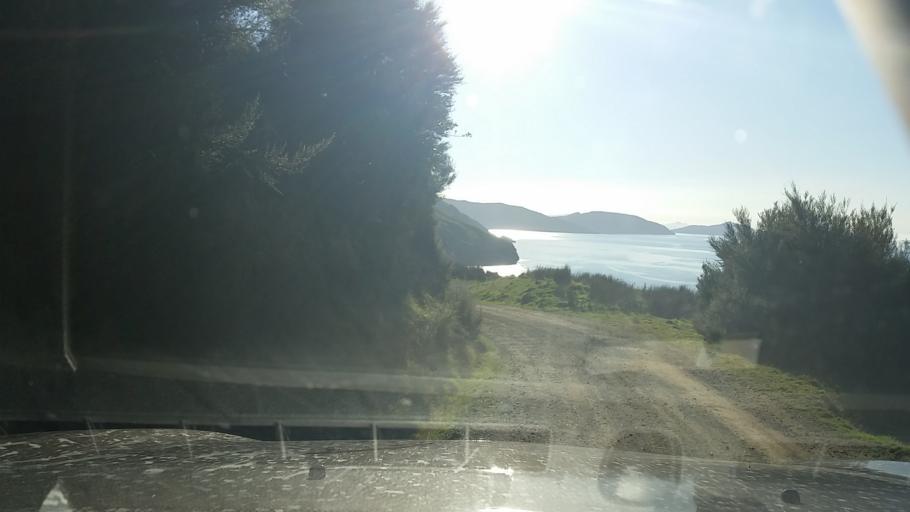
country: NZ
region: Marlborough
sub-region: Marlborough District
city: Picton
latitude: -41.0215
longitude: 174.1412
